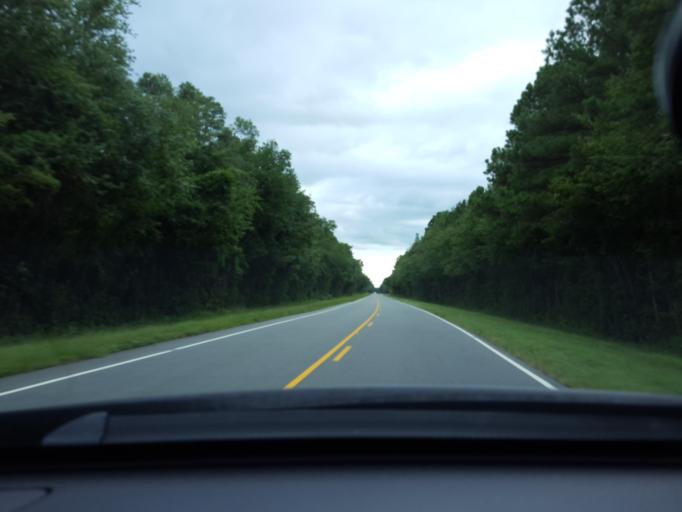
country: US
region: North Carolina
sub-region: Bladen County
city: Elizabethtown
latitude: 34.7000
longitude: -78.4772
